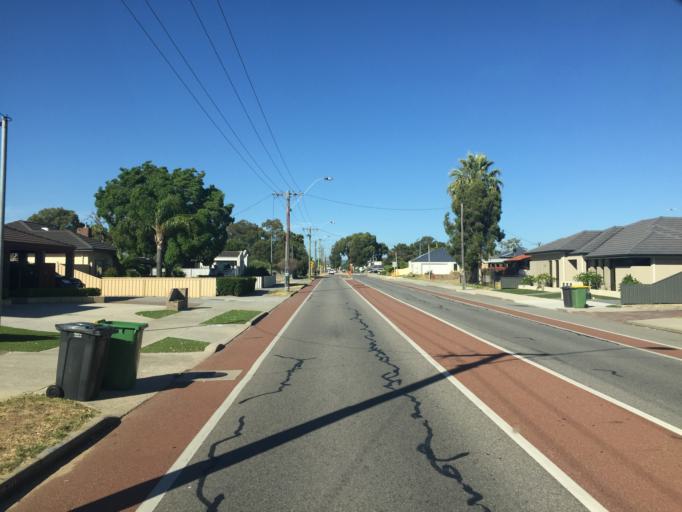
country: AU
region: Western Australia
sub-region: Canning
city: East Cannington
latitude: -32.0154
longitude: 115.9632
